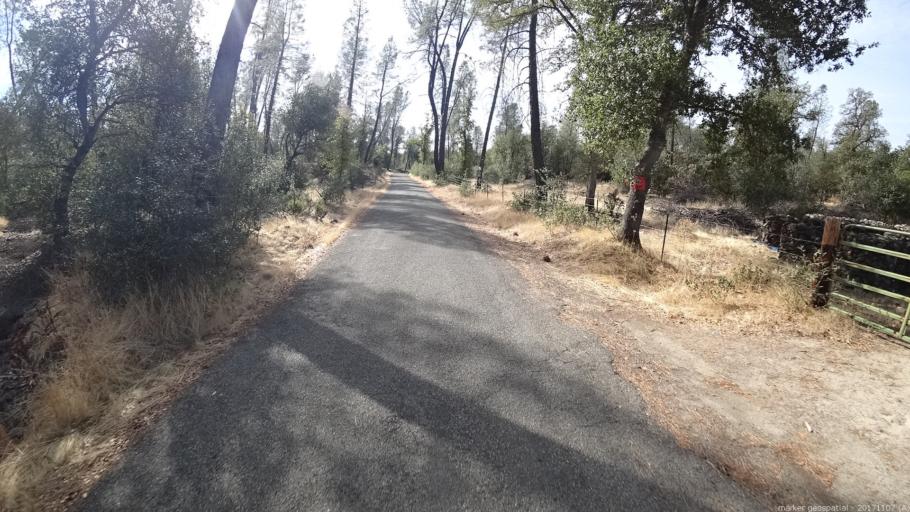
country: US
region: California
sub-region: Shasta County
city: Shasta
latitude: 40.4159
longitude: -122.5298
